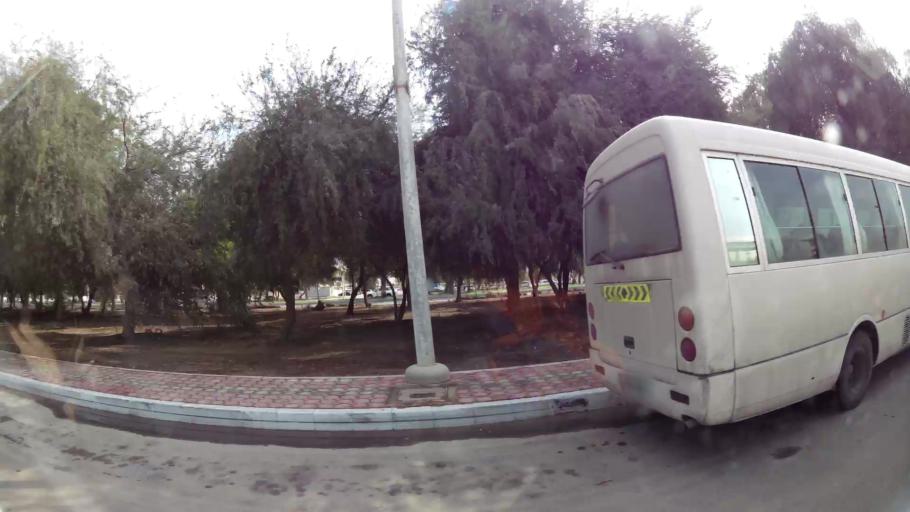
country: AE
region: Abu Dhabi
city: Abu Dhabi
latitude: 24.4390
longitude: 54.4303
